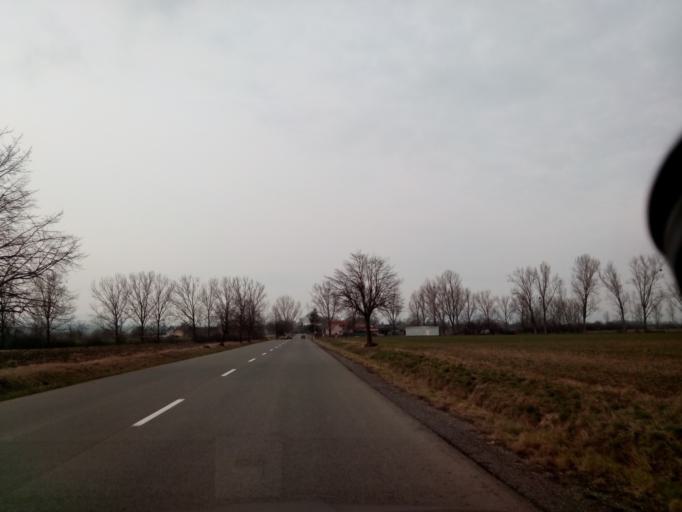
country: SK
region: Kosicky
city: Trebisov
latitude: 48.5537
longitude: 21.6799
